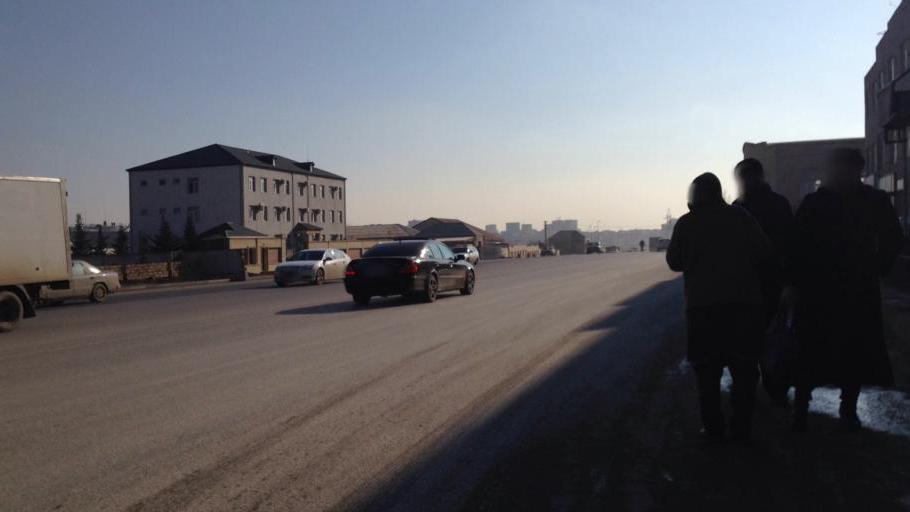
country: AZ
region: Baki
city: Sabuncu
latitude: 40.4452
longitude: 49.9340
